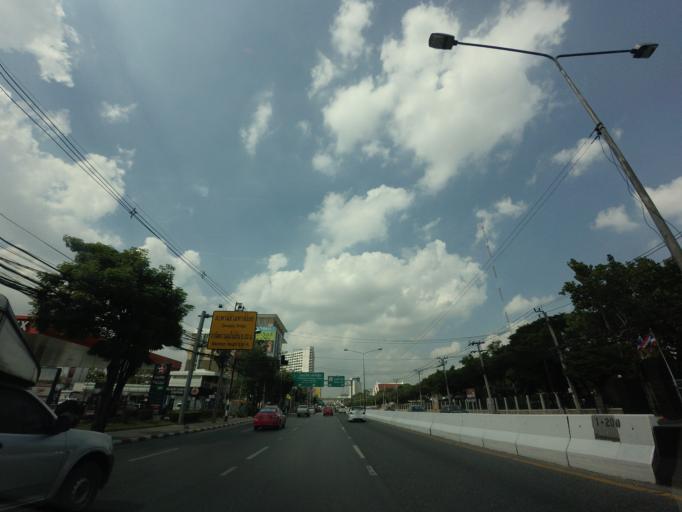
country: TH
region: Bangkok
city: Chatuchak
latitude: 13.8450
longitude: 100.5660
